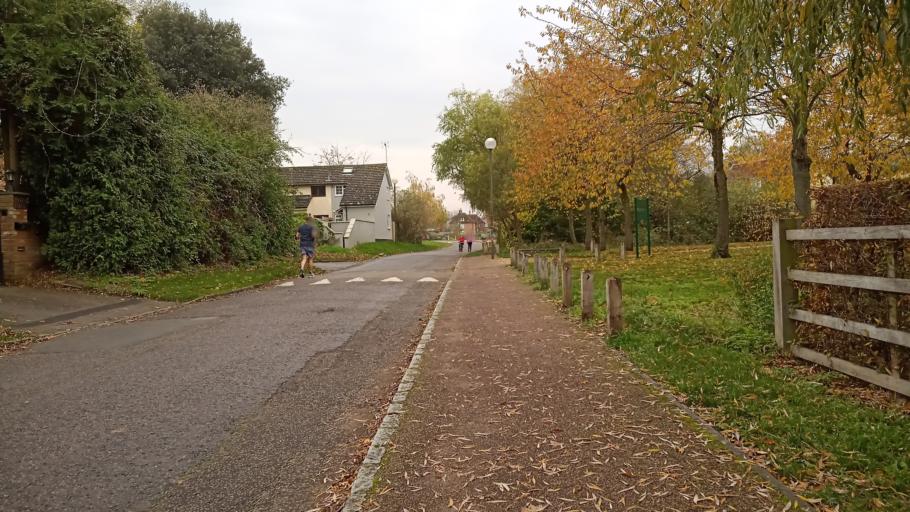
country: GB
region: England
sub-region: Milton Keynes
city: Shenley Church End
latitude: 52.0113
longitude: -0.7842
